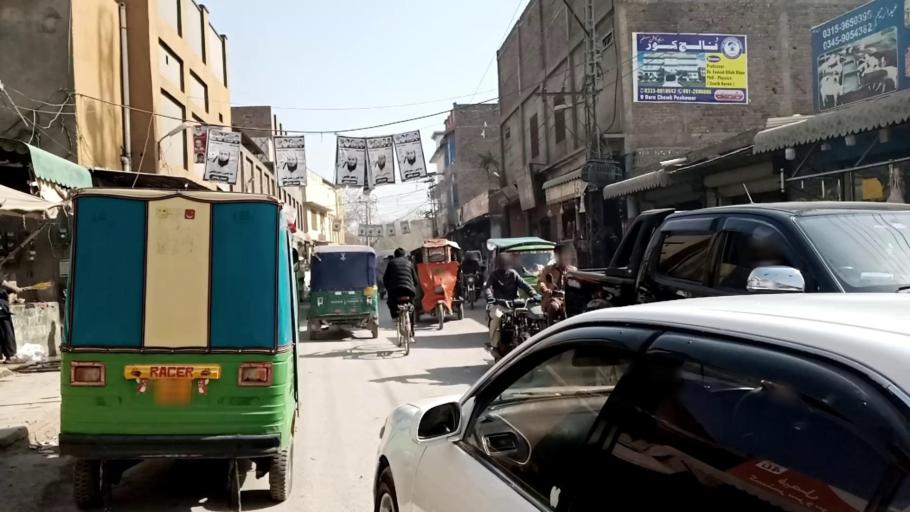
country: PK
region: Khyber Pakhtunkhwa
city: Peshawar
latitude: 33.9957
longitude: 71.5781
